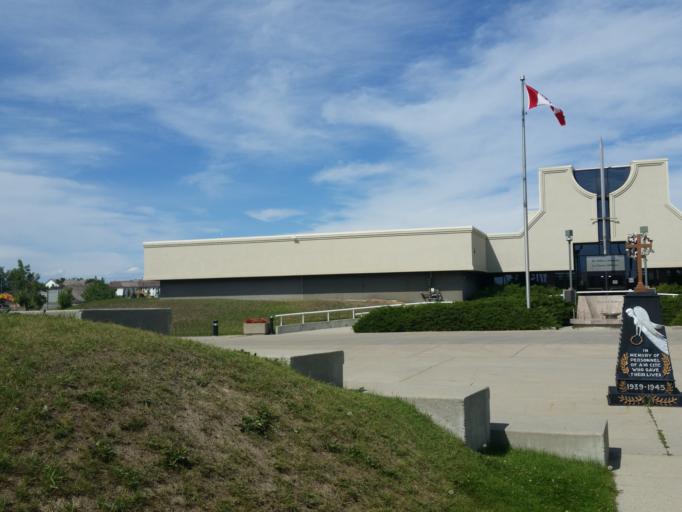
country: CA
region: Alberta
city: Calgary
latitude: 51.0134
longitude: -114.1169
